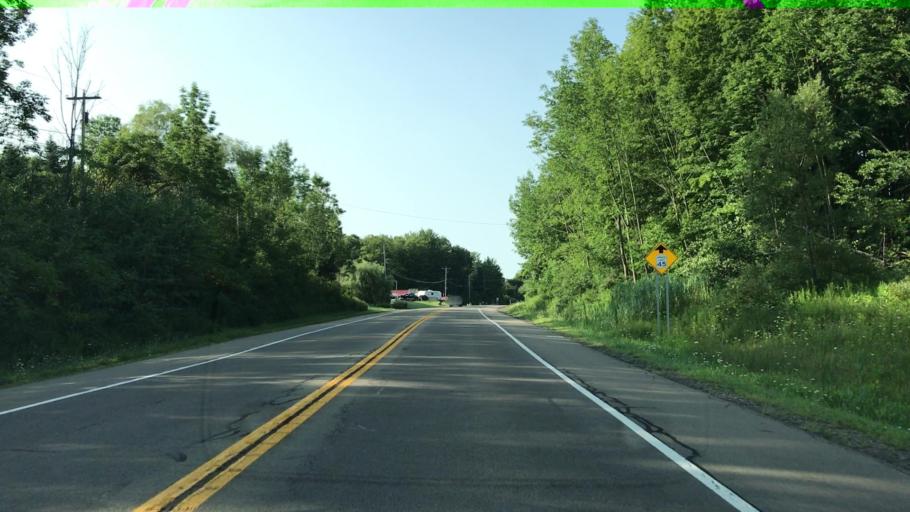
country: US
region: New York
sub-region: Chautauqua County
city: Fredonia
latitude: 42.3618
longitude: -79.3113
